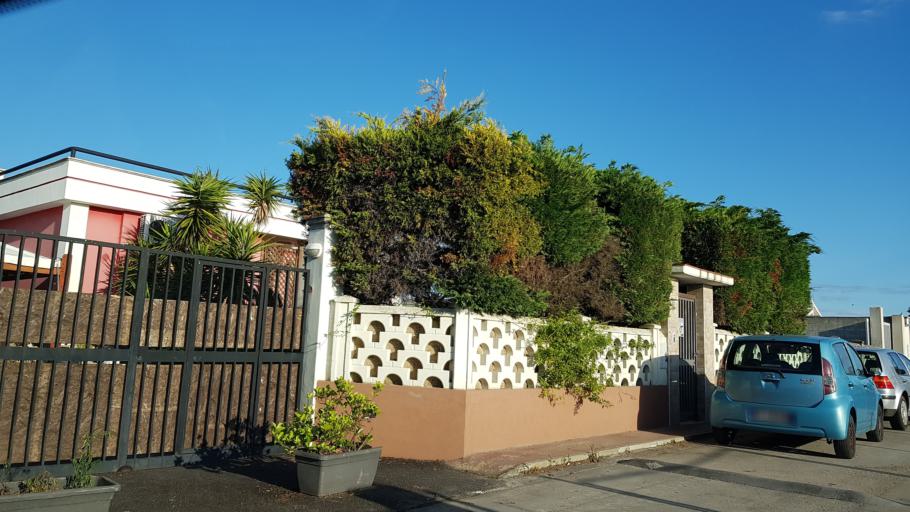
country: IT
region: Apulia
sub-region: Provincia di Brindisi
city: Brindisi
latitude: 40.6147
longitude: 17.9237
